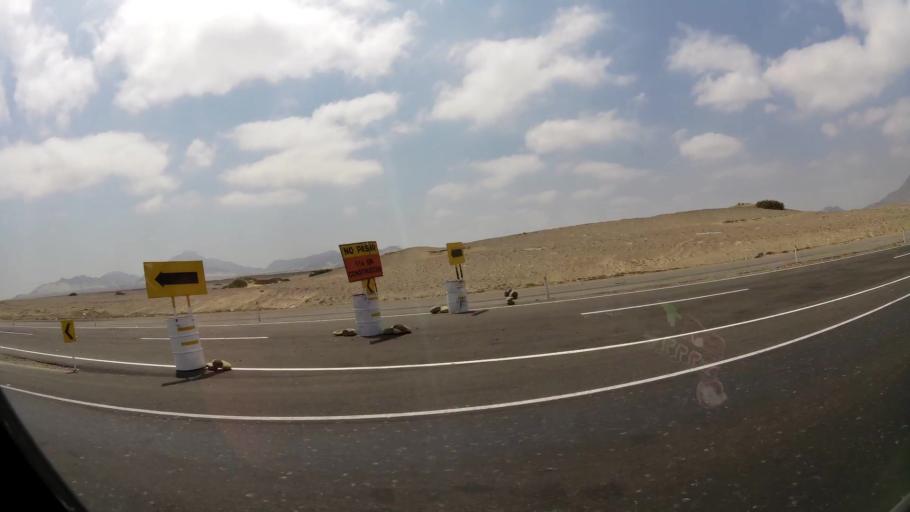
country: PE
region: La Libertad
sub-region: Ascope
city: Paijan
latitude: -7.6509
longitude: -79.3457
